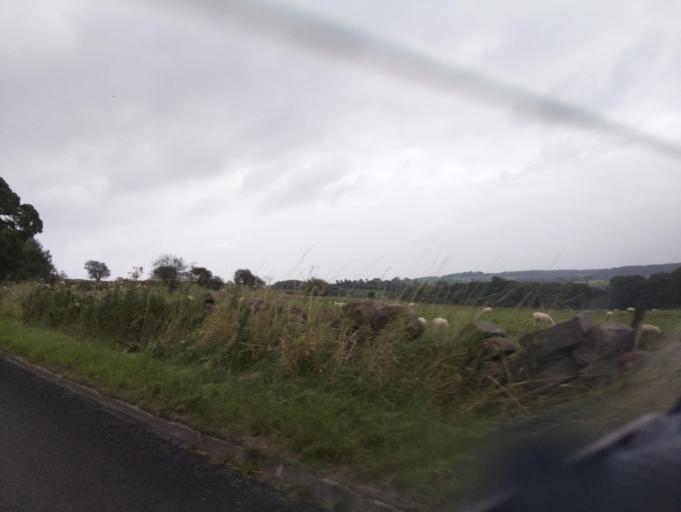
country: GB
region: England
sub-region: Staffordshire
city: Cheadle
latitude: 53.0323
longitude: -1.9146
